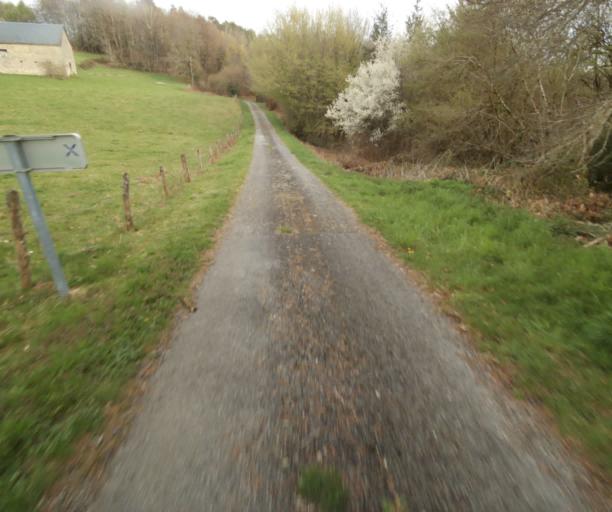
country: FR
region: Limousin
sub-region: Departement de la Correze
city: Argentat
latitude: 45.2098
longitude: 1.9889
